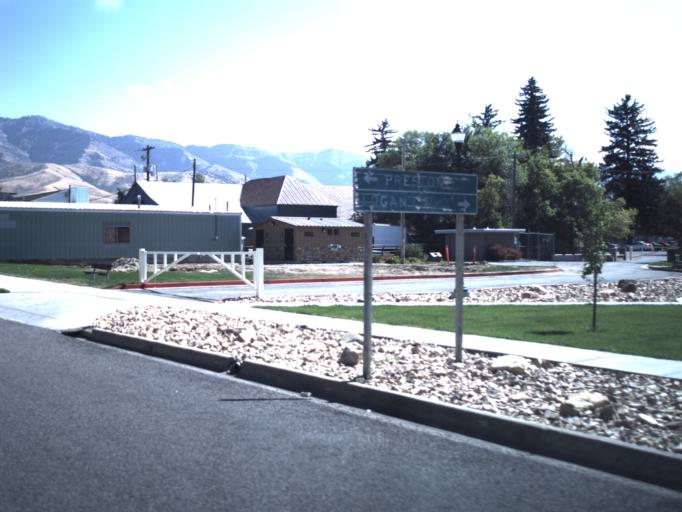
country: US
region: Utah
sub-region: Cache County
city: Smithfield
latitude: 41.8386
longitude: -111.8347
